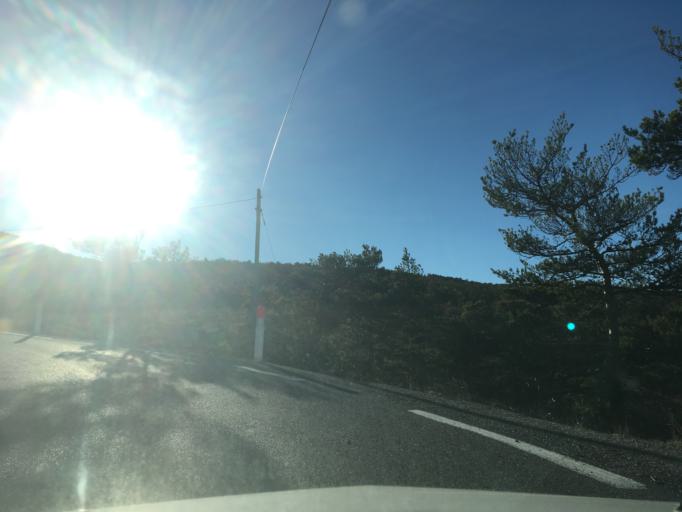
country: FR
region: Provence-Alpes-Cote d'Azur
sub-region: Departement des Alpes-de-Haute-Provence
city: Castellane
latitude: 43.7467
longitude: 6.4349
